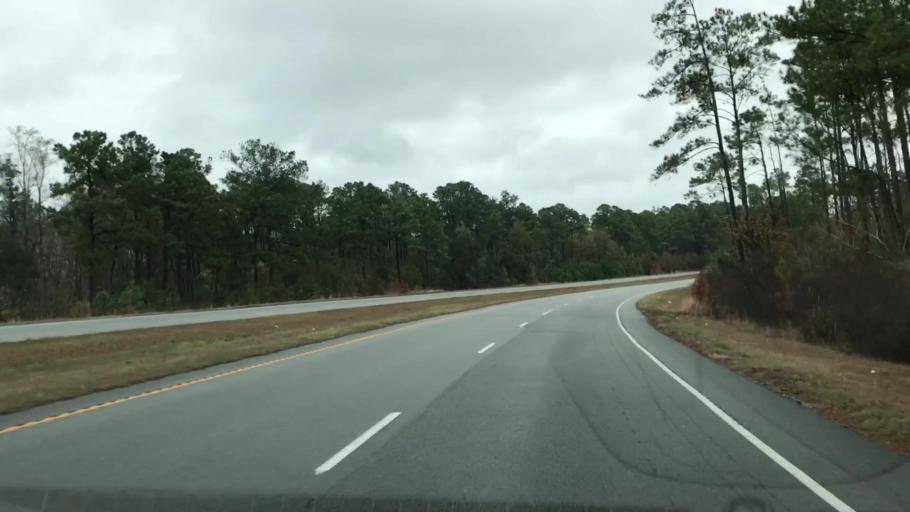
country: US
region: South Carolina
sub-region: Georgetown County
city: Georgetown
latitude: 33.1792
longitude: -79.4134
